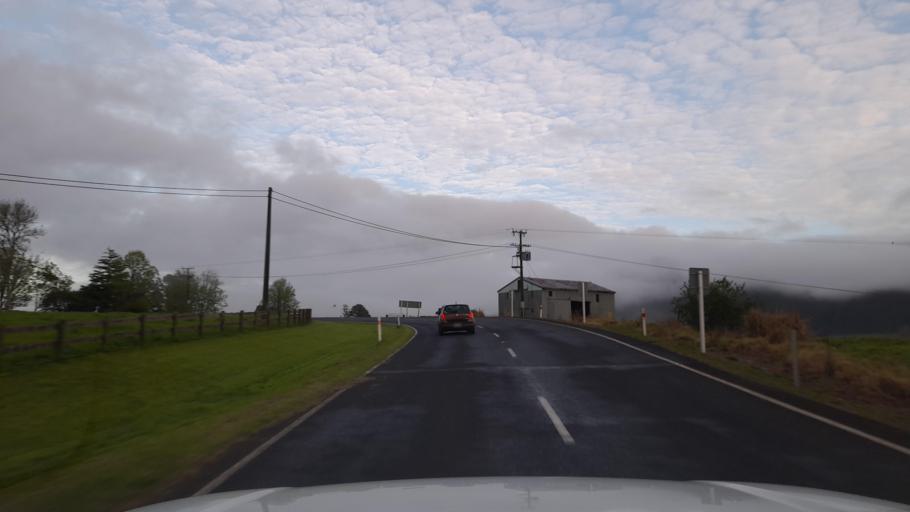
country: NZ
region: Northland
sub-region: Whangarei
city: Maungatapere
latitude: -35.7083
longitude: 173.9774
